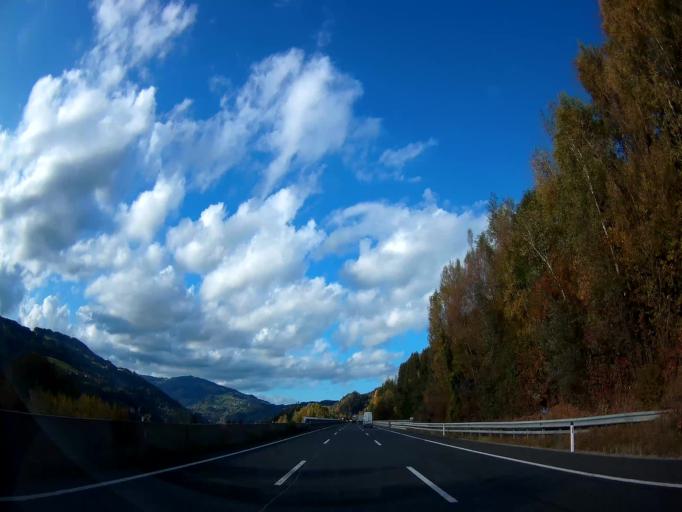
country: AT
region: Carinthia
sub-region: Politischer Bezirk Wolfsberg
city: Wolfsberg
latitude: 46.8760
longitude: 14.8322
